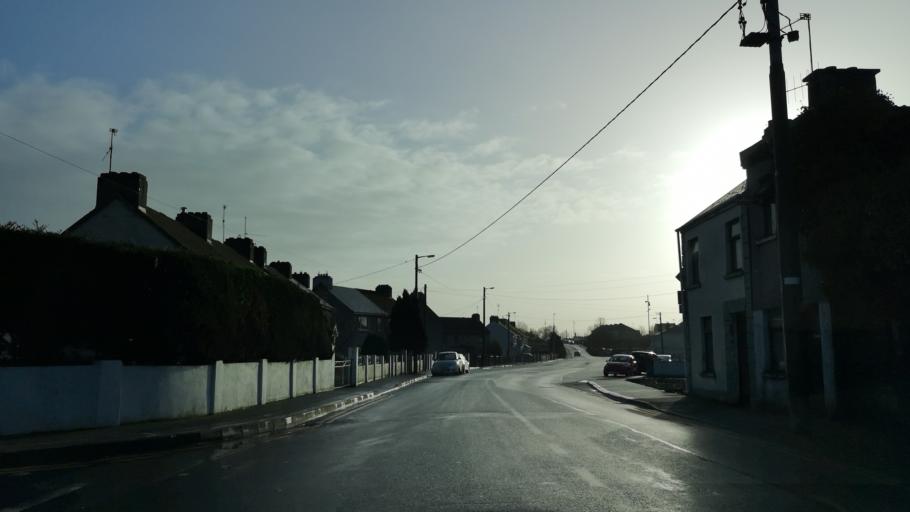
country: IE
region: Connaught
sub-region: County Galway
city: Tuam
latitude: 53.5109
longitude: -8.8561
